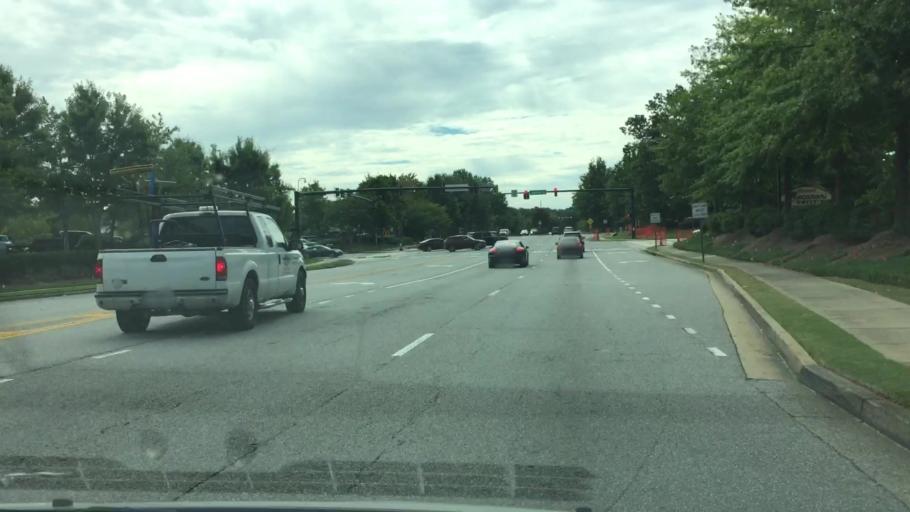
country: US
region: Georgia
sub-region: Fulton County
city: Alpharetta
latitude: 34.0927
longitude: -84.2774
